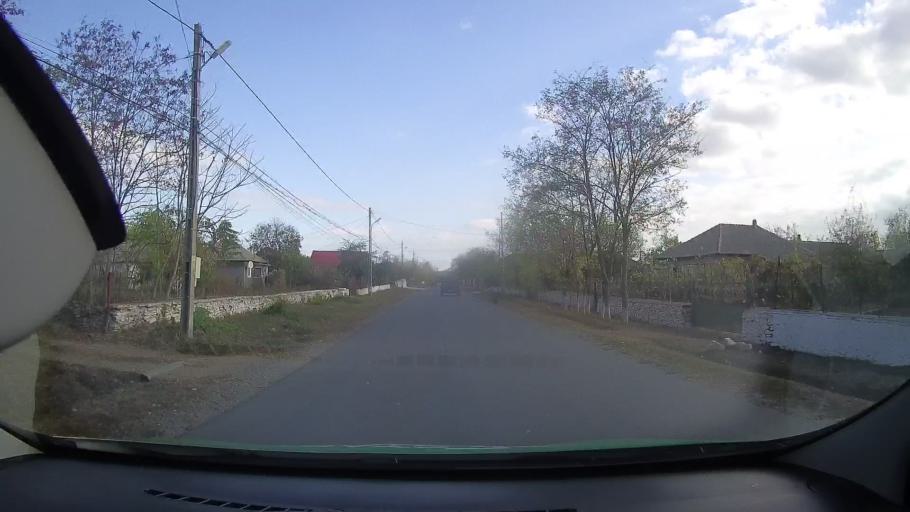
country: RO
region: Constanta
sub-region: Comuna Sacele
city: Sacele
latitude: 44.4885
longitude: 28.6390
